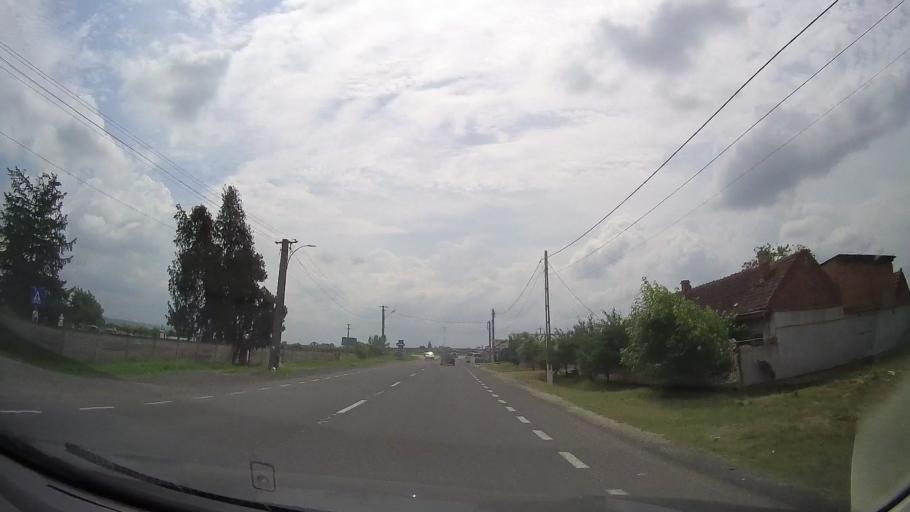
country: RO
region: Timis
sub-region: Comuna Costeiu
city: Costeiu
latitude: 45.7289
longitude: 21.8693
